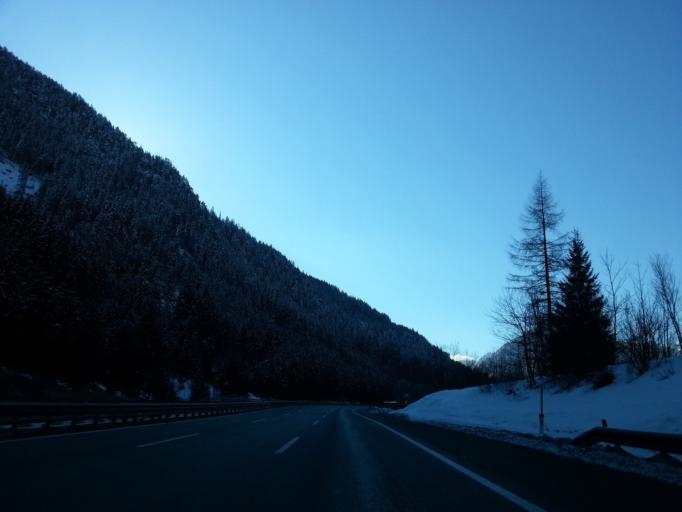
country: AT
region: Salzburg
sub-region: Politischer Bezirk Sankt Johann im Pongau
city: Flachau
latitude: 47.3181
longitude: 13.3951
